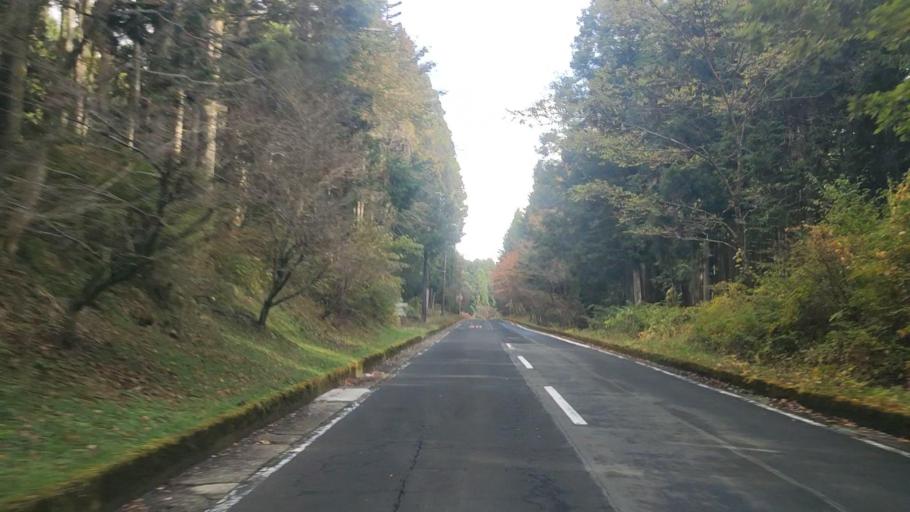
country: JP
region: Shizuoka
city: Fujinomiya
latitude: 35.3044
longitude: 138.6754
